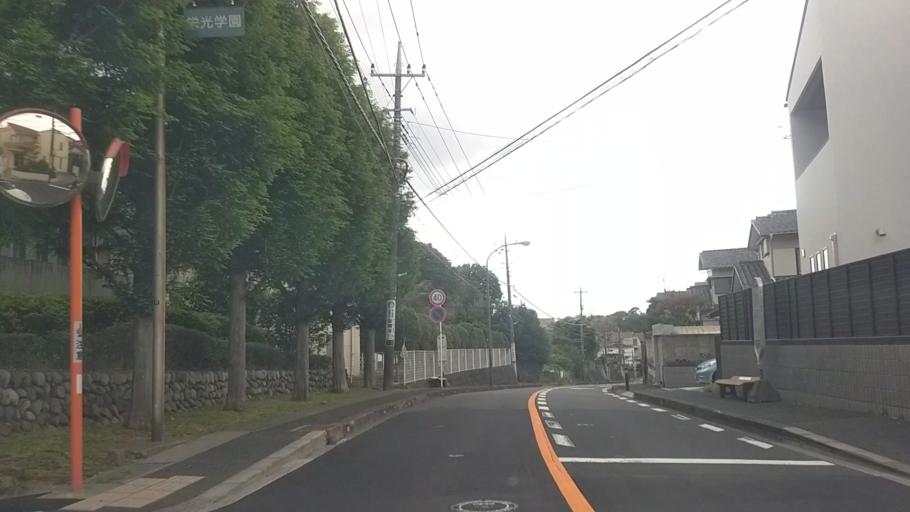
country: JP
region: Kanagawa
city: Fujisawa
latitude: 35.3566
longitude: 139.5206
